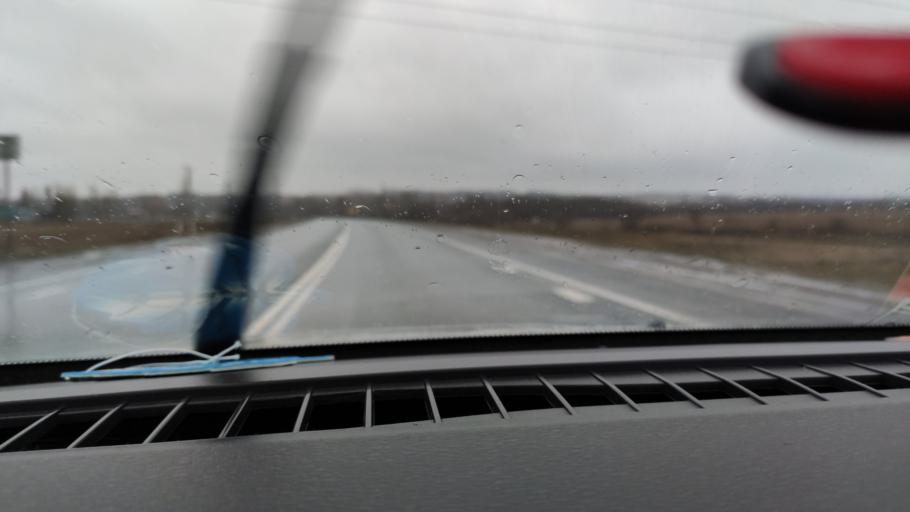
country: RU
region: Tatarstan
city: Mendeleyevsk
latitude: 55.8624
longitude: 52.2131
